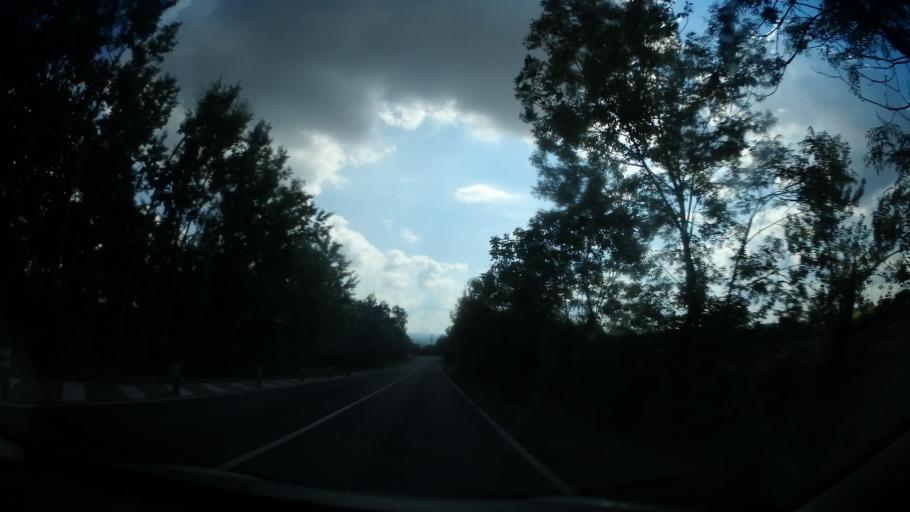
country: CZ
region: Central Bohemia
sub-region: Okres Benesov
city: Pysely
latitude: 49.8949
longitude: 14.7125
